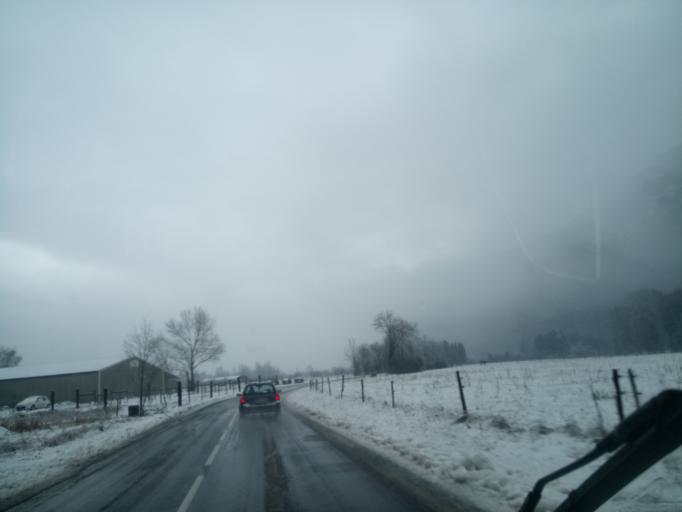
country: FR
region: Rhone-Alpes
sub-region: Departement de la Savoie
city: Saint-Etienne-de-Cuines
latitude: 45.3750
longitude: 6.2750
